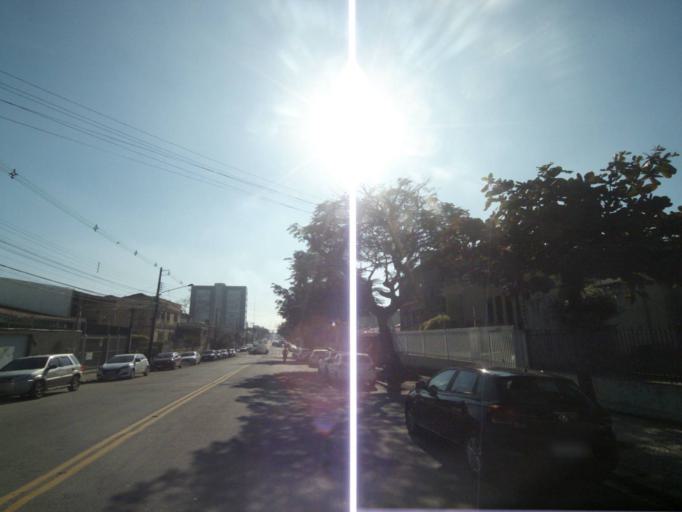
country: BR
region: Parana
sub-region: Paranagua
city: Paranagua
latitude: -25.5175
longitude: -48.5118
